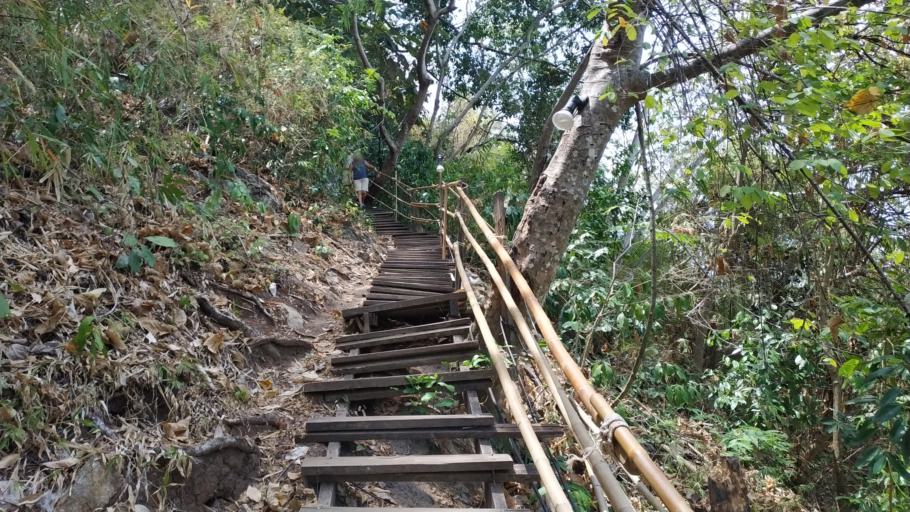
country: TH
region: Phangnga
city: Ban Ao Nang
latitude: 8.0264
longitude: 98.8269
